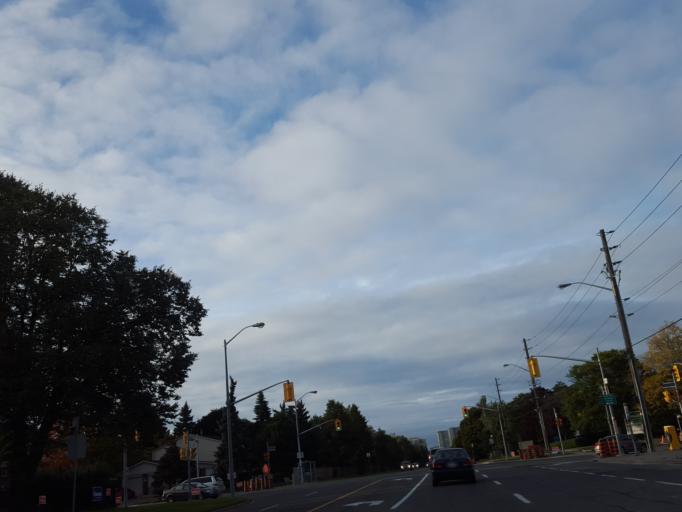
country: CA
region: Ontario
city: Scarborough
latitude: 43.7850
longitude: -79.3107
